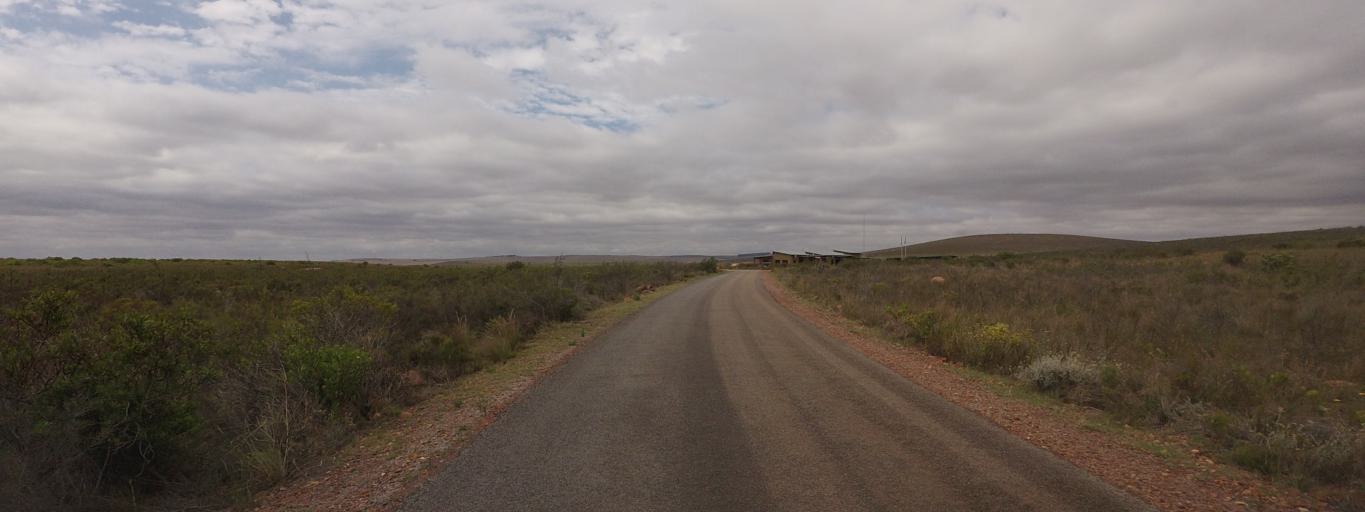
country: ZA
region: Western Cape
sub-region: Overberg District Municipality
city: Swellendam
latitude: -34.0579
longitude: 20.4311
